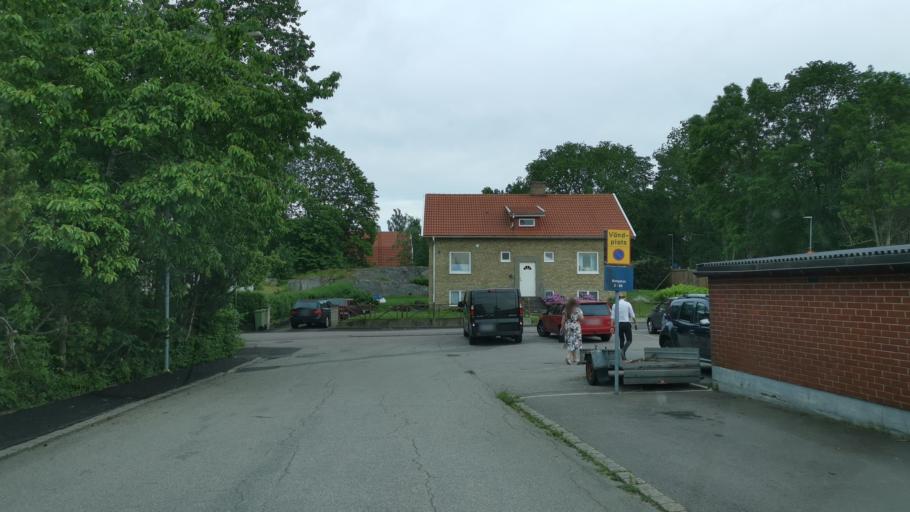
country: SE
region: Vaestra Goetaland
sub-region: Vanersborgs Kommun
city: Vanersborg
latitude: 58.3607
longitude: 12.3484
